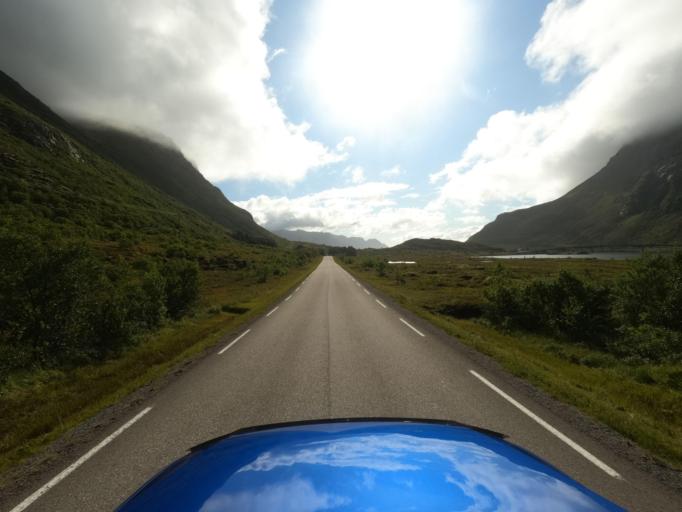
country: NO
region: Nordland
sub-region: Vagan
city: Kabelvag
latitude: 68.2758
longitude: 14.1636
